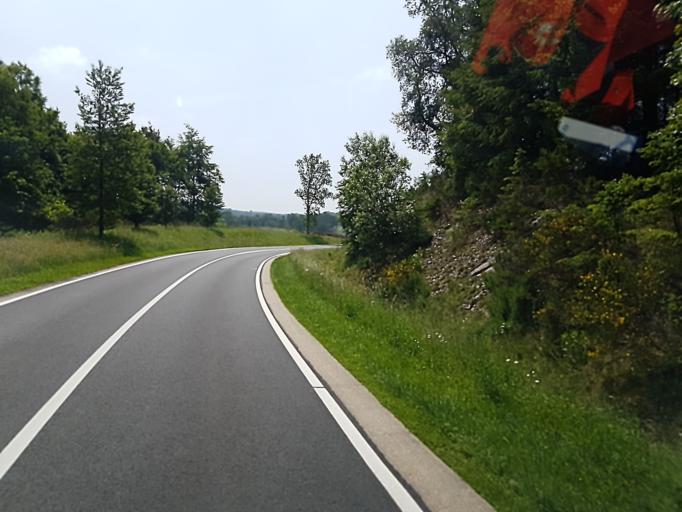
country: BE
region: Wallonia
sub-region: Province de Liege
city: Lierneux
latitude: 50.3438
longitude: 5.8066
